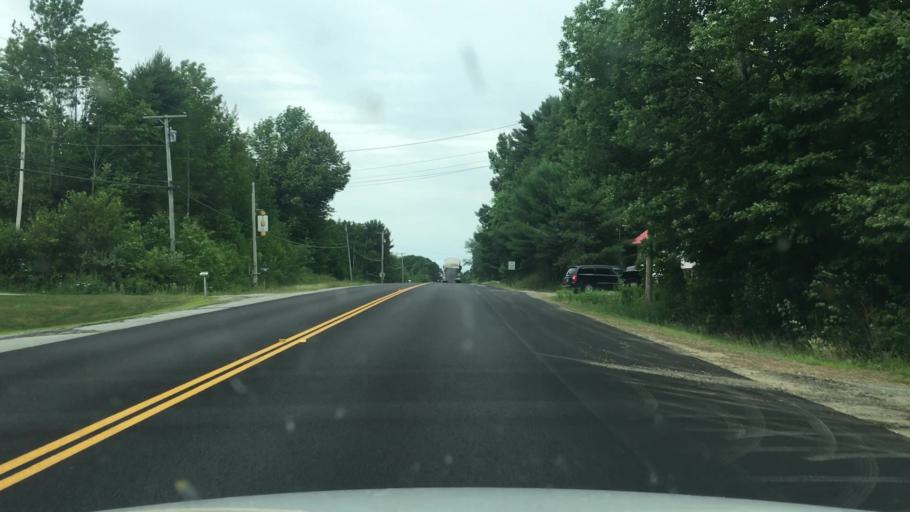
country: US
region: Maine
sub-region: Waldo County
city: Palermo
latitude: 44.3899
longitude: -69.4677
